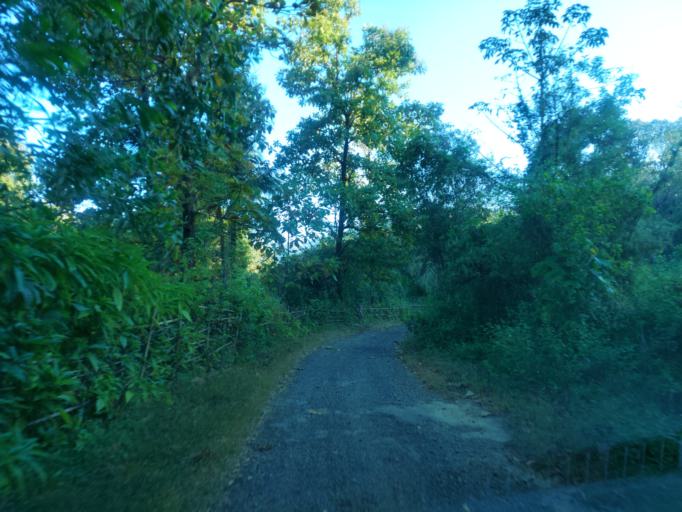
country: IN
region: Maharashtra
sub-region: Sindhudurg
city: Kudal
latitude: 16.0712
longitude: 73.8250
